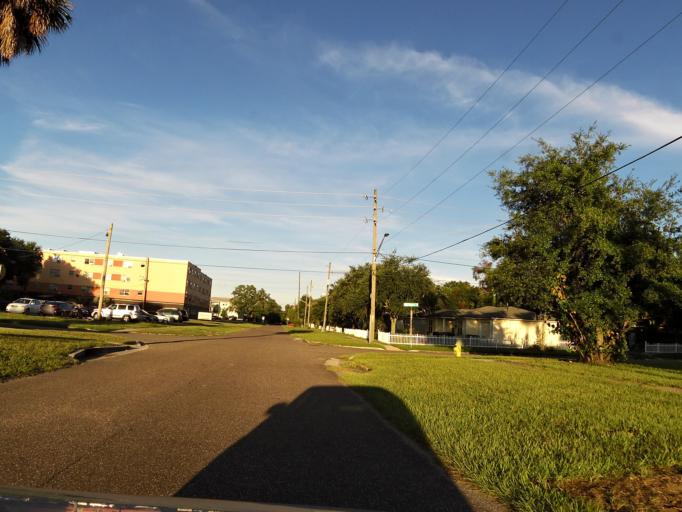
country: US
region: Florida
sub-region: Duval County
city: Jacksonville
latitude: 30.3328
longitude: -81.6413
